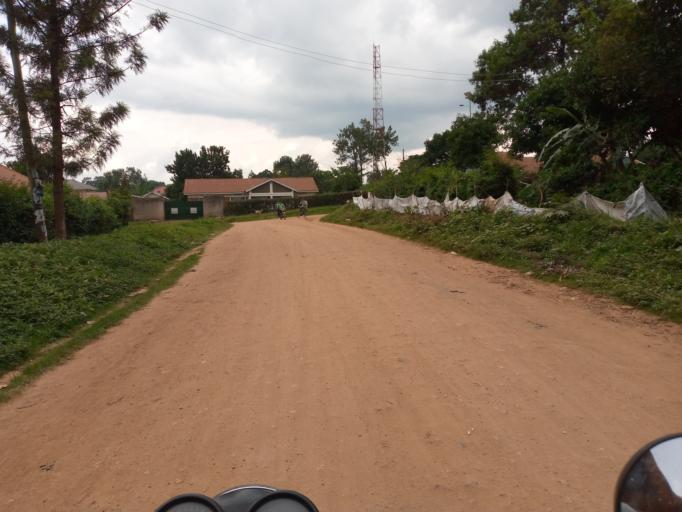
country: UG
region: Eastern Region
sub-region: Mbale District
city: Mbale
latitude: 1.0838
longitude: 34.1698
